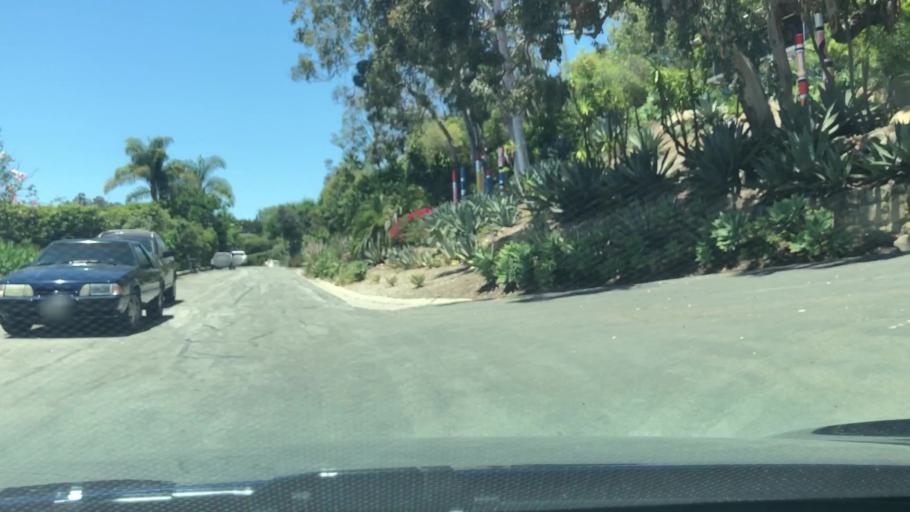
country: US
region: California
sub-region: Santa Barbara County
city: Santa Barbara
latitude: 34.4383
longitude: -119.6939
